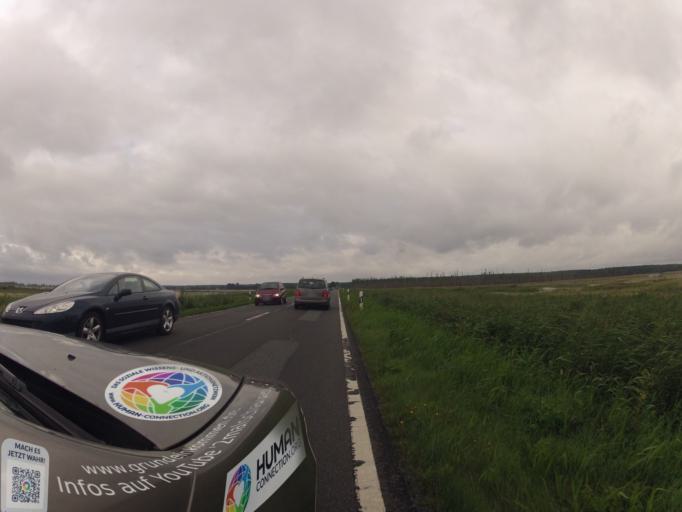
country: DE
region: Mecklenburg-Vorpommern
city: Lassan
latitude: 53.8710
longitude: 13.8121
